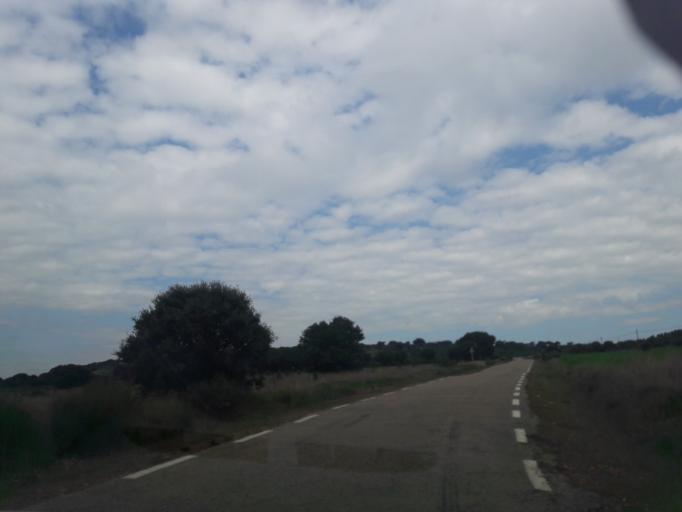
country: ES
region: Castille and Leon
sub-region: Provincia de Salamanca
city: Serradilla del Arroyo
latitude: 40.5226
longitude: -6.3788
